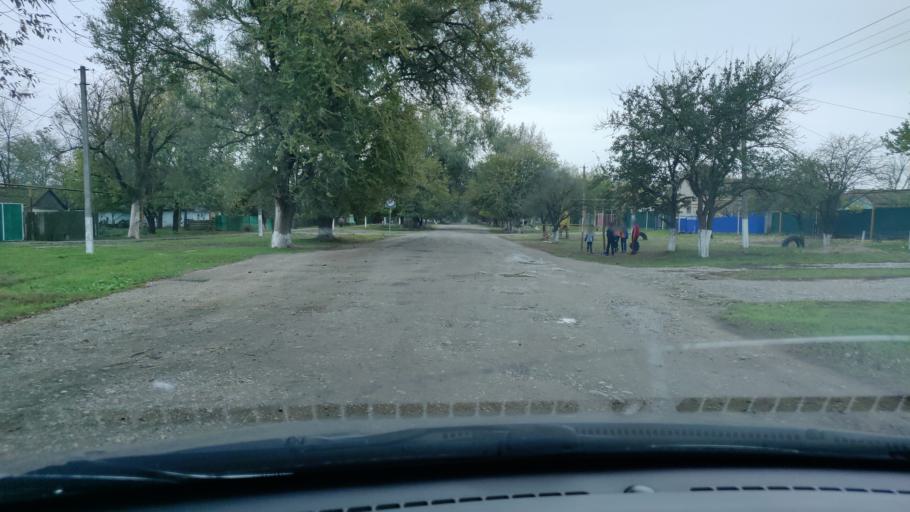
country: RU
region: Stavropol'skiy
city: Irgakly
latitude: 44.2439
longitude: 44.7204
